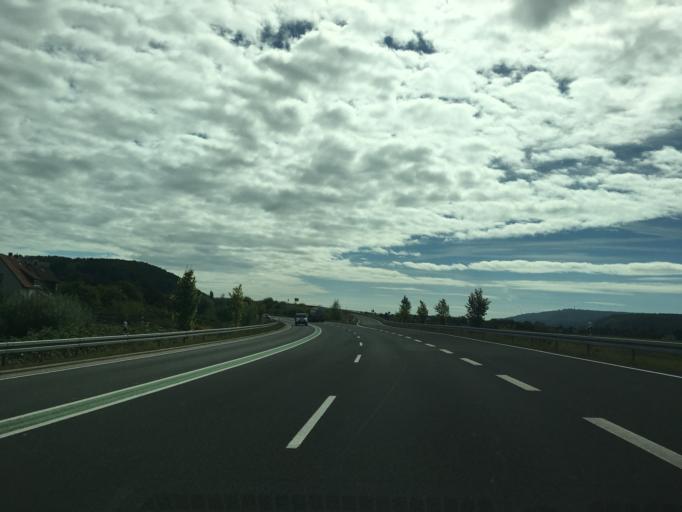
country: DE
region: Lower Saxony
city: Hessisch Oldendorf
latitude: 52.1344
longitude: 9.2979
